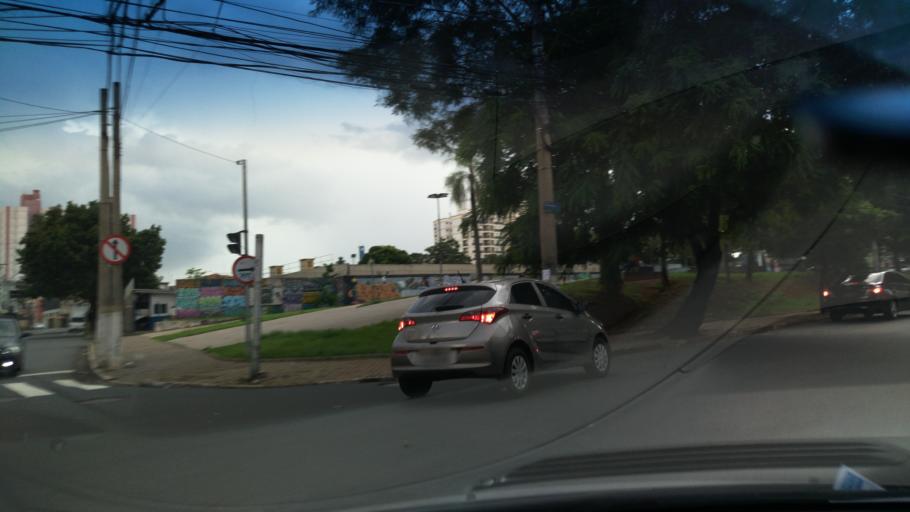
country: BR
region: Sao Paulo
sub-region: Campinas
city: Campinas
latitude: -22.9153
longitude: -47.0548
